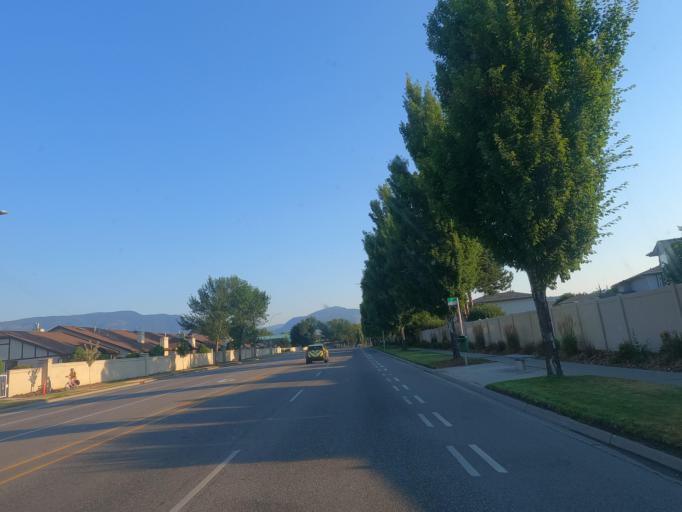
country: CA
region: British Columbia
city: Kelowna
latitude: 49.8731
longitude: -119.4761
